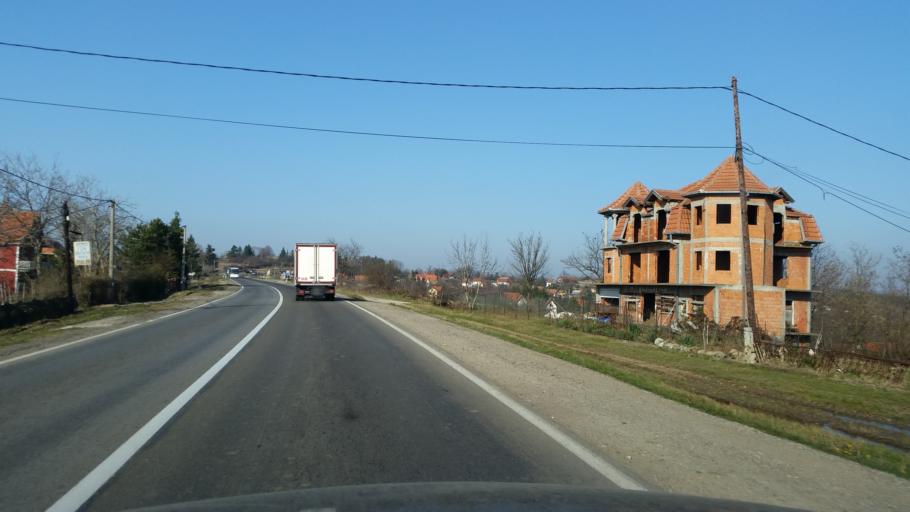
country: RS
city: Stepojevac
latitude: 44.5528
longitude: 20.3001
